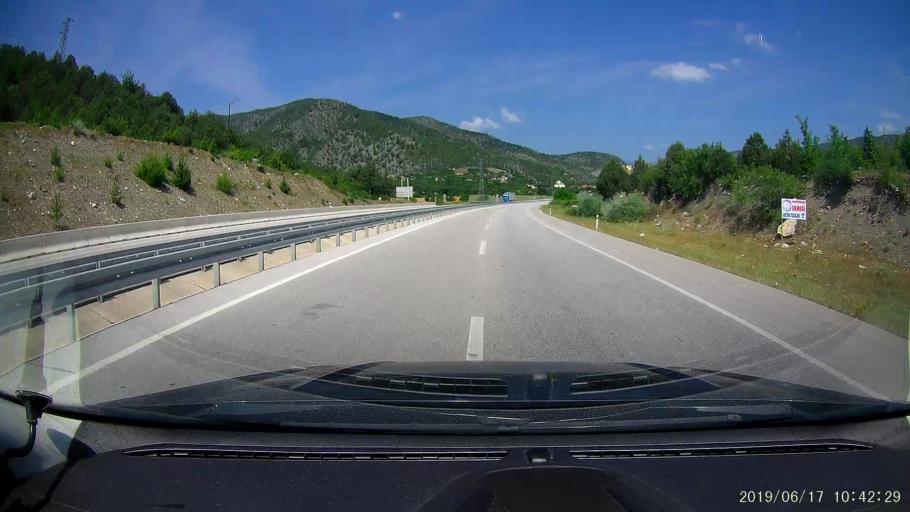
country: TR
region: Corum
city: Hacihamza
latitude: 41.0484
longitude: 34.5524
